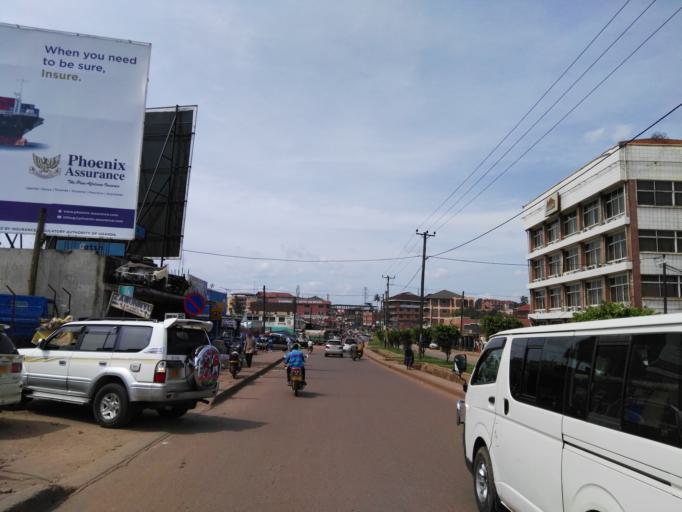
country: UG
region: Central Region
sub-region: Kampala District
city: Kampala
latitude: 0.2981
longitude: 32.5746
